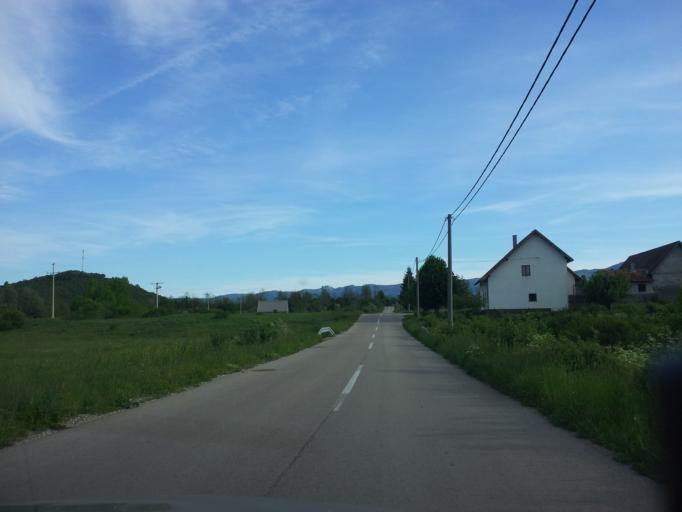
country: HR
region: Zadarska
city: Obrovac
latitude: 44.3860
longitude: 15.6782
